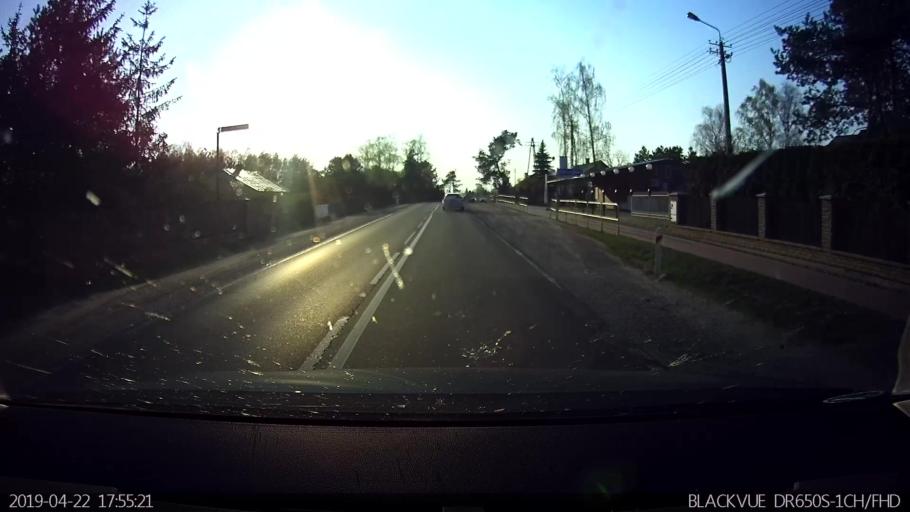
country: PL
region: Masovian Voivodeship
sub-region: Powiat wegrowski
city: Stoczek
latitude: 52.4614
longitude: 21.9194
